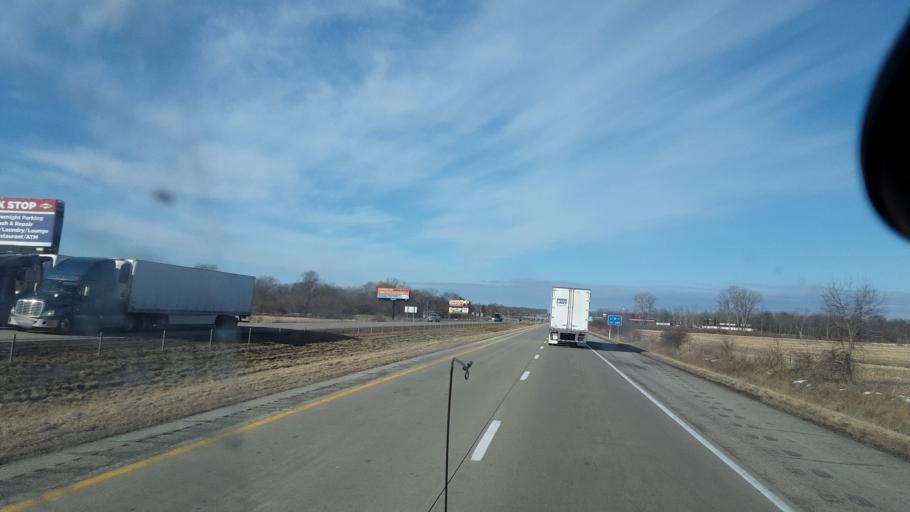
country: US
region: Indiana
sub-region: Wayne County
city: Centerville
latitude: 39.8590
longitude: -84.9836
